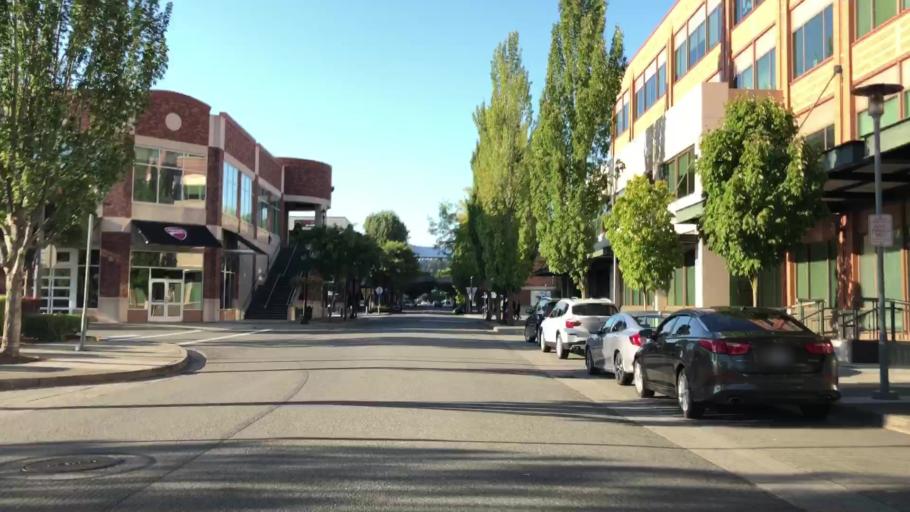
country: US
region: Washington
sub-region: King County
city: Redmond
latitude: 47.6692
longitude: -122.1190
